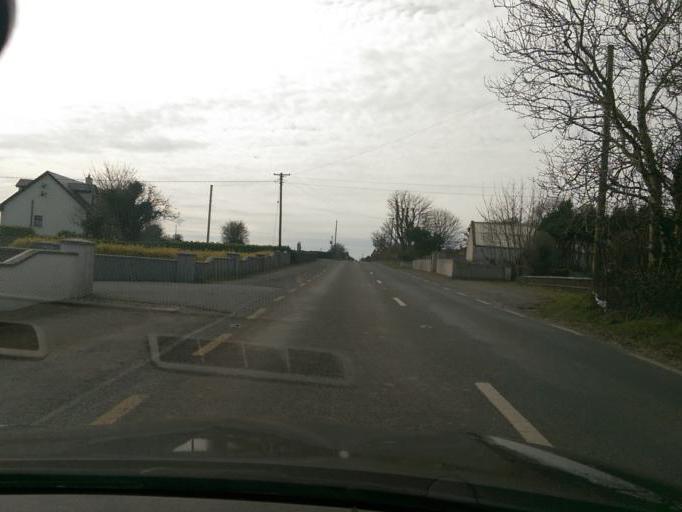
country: IE
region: Connaught
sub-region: County Galway
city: Claregalway
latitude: 53.3730
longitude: -8.8816
